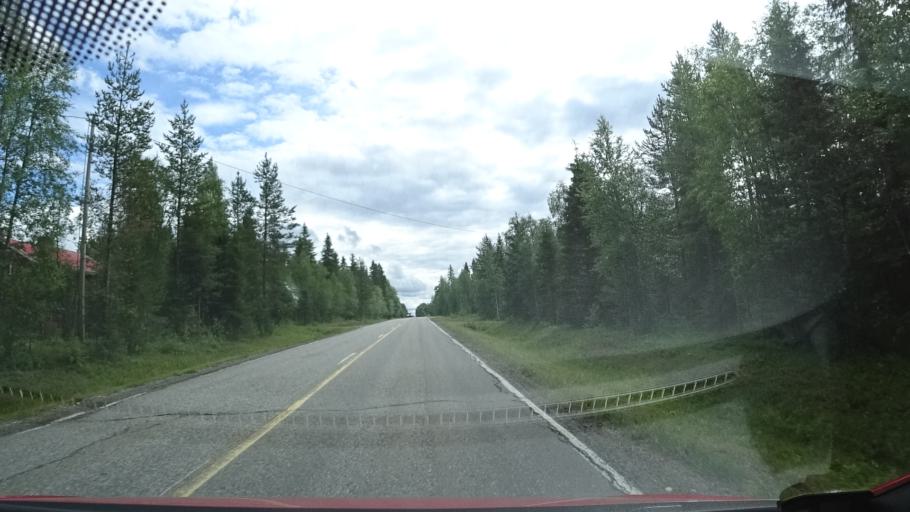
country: FI
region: Lapland
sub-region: Tunturi-Lappi
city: Kittilae
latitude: 67.4740
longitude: 24.9382
